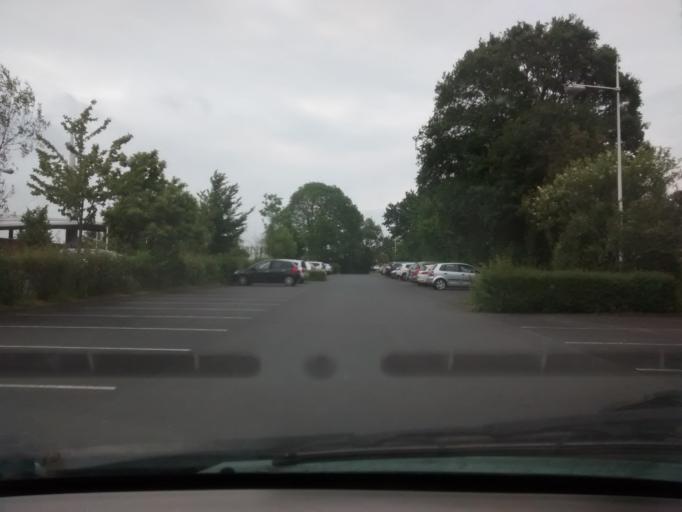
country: FR
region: Lower Normandy
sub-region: Departement de la Manche
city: Saint-Lo
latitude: 49.1043
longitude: -1.0735
